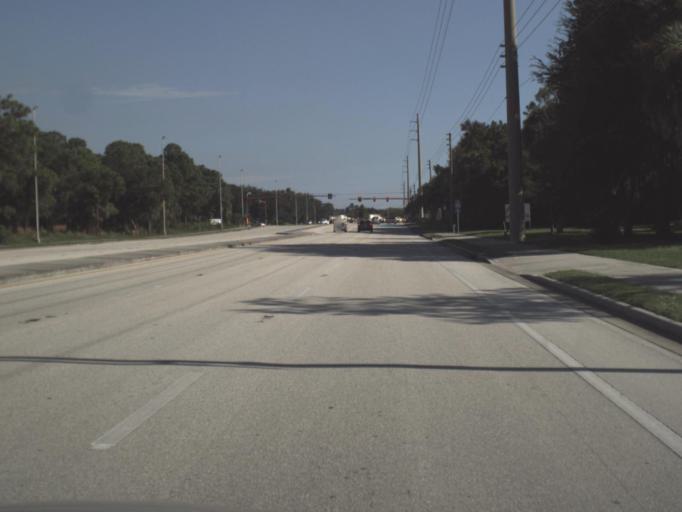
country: US
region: Florida
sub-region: Sarasota County
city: South Venice
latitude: 27.0429
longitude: -82.4016
